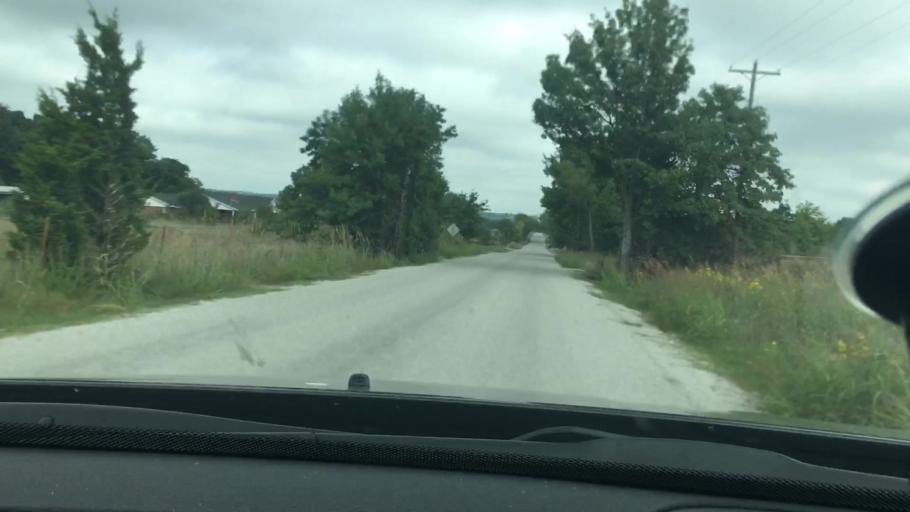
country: US
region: Oklahoma
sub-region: Carter County
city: Lone Grove
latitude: 34.1247
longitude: -97.2128
